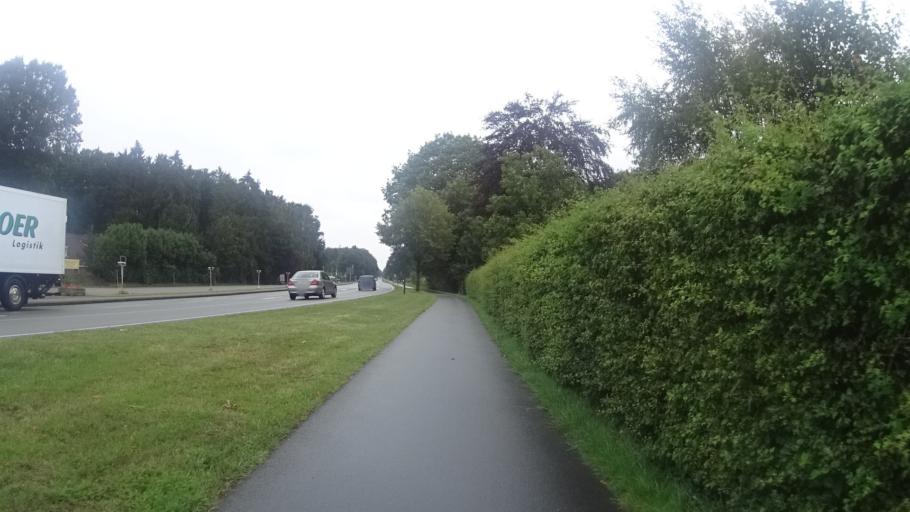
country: DE
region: Lower Saxony
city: Holtland
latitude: 53.2796
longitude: 7.5754
